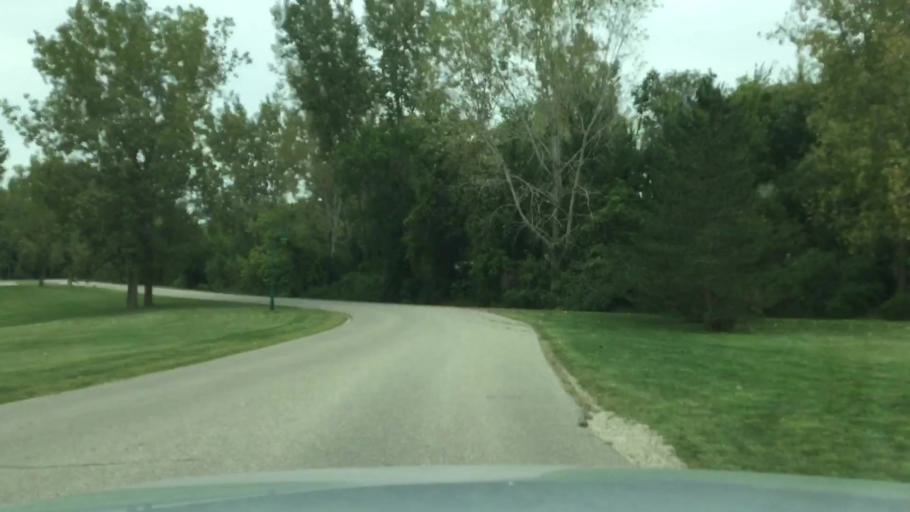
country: US
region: Michigan
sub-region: Shiawassee County
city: Durand
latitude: 42.9518
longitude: -83.9559
